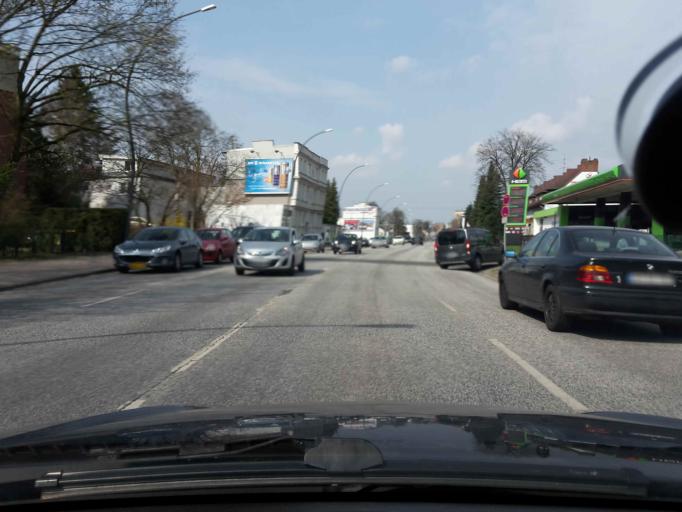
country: DE
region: Hamburg
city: Eidelstedt
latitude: 53.5856
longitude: 9.8792
